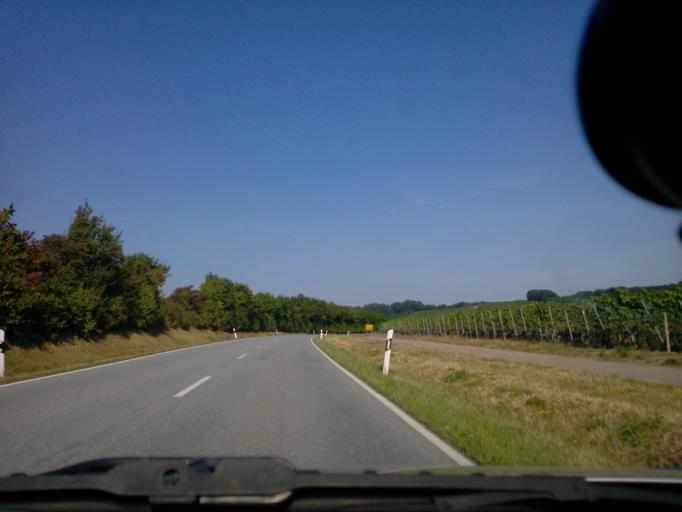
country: DE
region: Baden-Wuerttemberg
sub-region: Regierungsbezirk Stuttgart
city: Brackenheim
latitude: 49.0973
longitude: 9.0333
